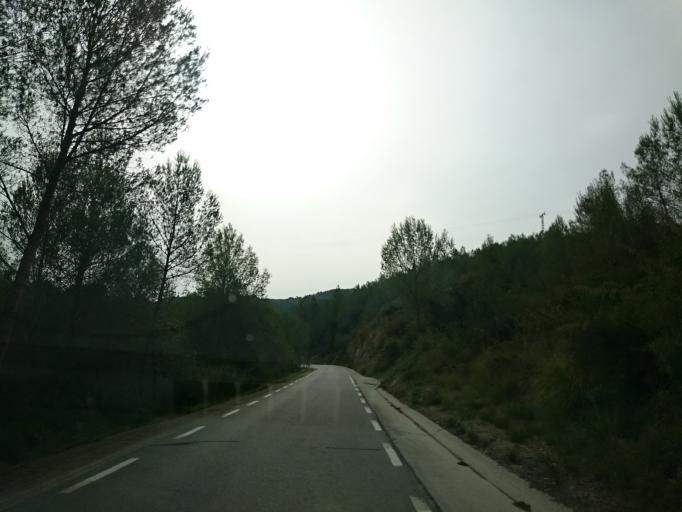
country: ES
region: Catalonia
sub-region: Provincia de Barcelona
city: Olivella
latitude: 41.3097
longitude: 1.7994
